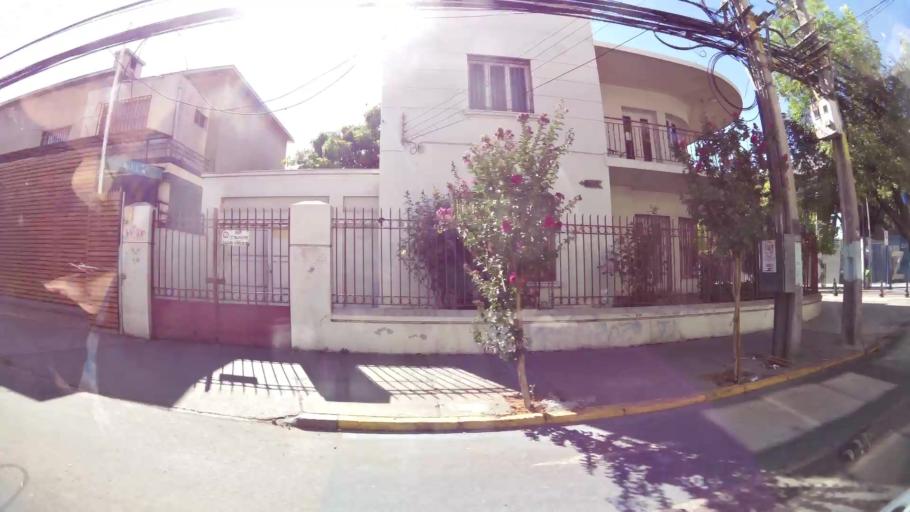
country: CL
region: O'Higgins
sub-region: Provincia de Cachapoal
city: Rancagua
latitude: -34.1704
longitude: -70.7379
